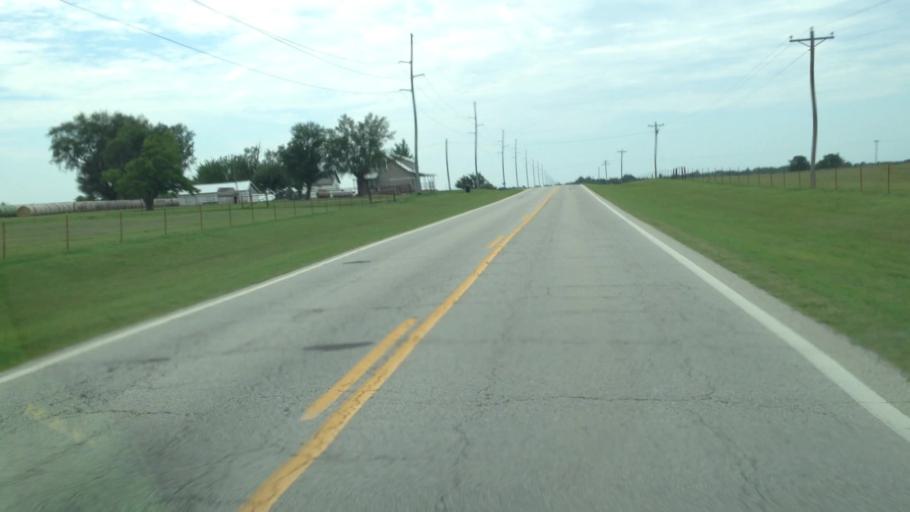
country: US
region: Kansas
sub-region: Labette County
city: Chetopa
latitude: 36.9143
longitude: -95.0896
